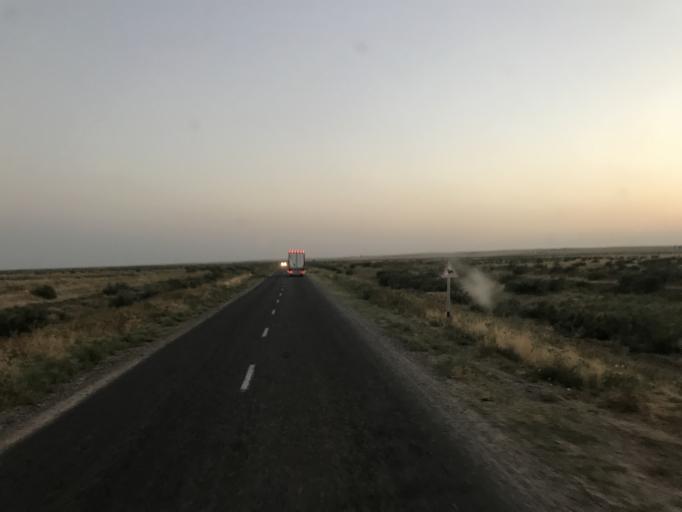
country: UZ
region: Toshkent
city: Chinoz
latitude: 41.2138
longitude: 68.5983
